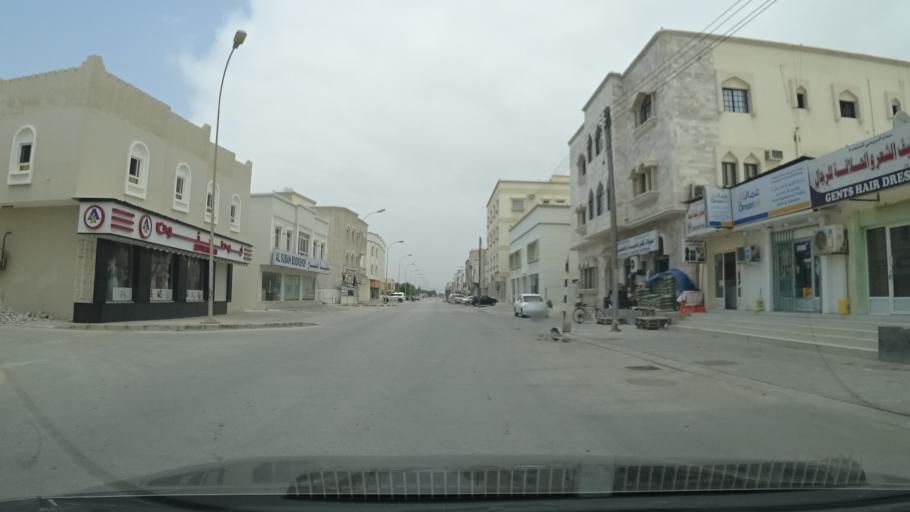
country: OM
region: Zufar
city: Salalah
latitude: 17.0222
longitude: 54.1592
